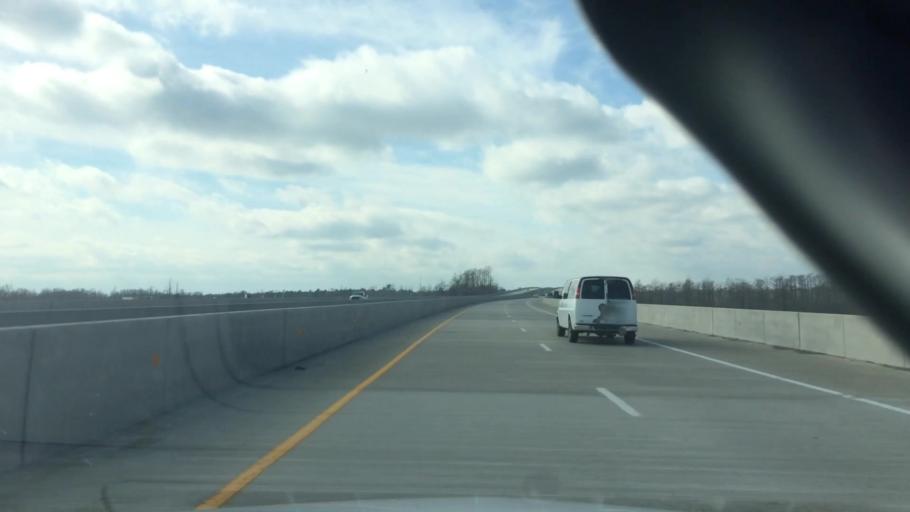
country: US
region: North Carolina
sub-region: Brunswick County
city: Navassa
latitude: 34.2735
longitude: -77.9935
